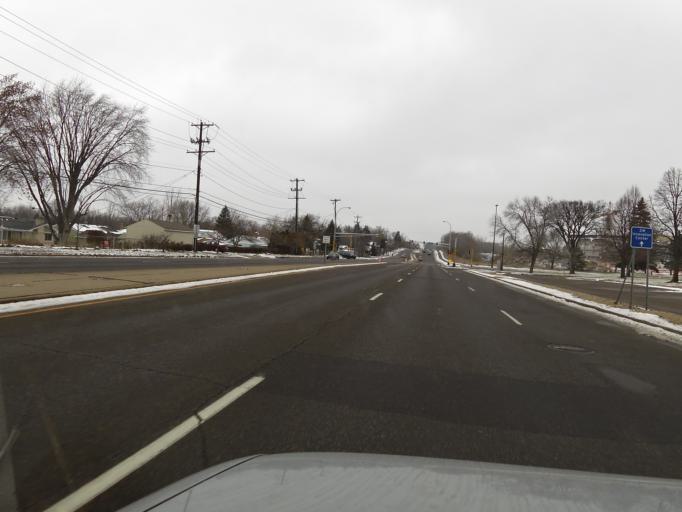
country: US
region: Minnesota
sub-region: Ramsey County
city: Maplewood
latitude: 44.9547
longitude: -93.0049
